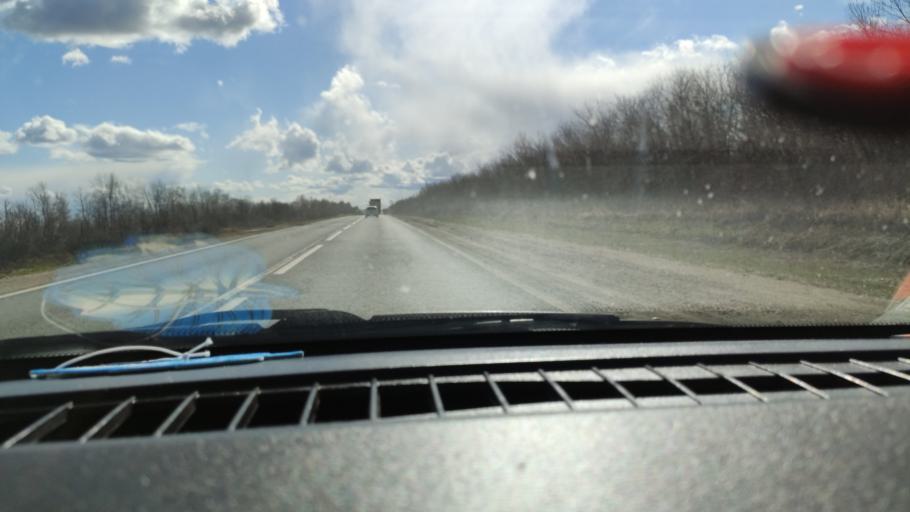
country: RU
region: Saratov
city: Dukhovnitskoye
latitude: 52.6839
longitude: 48.2360
